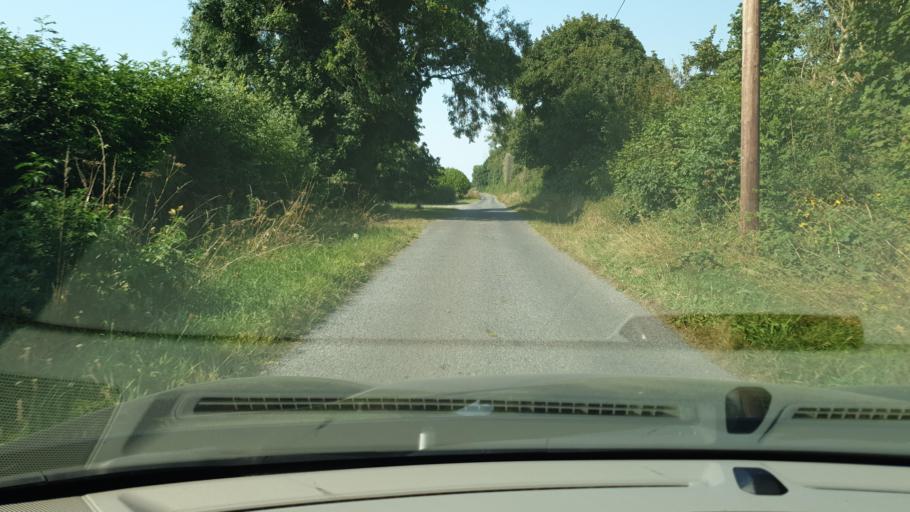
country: IE
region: Leinster
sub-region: An Mhi
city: Athboy
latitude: 53.6056
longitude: -6.9882
